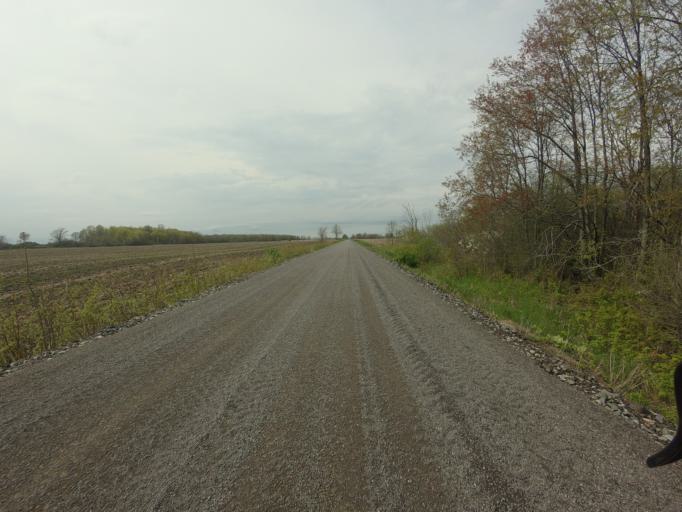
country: CA
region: Ontario
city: Carleton Place
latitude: 45.1722
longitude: -76.1520
